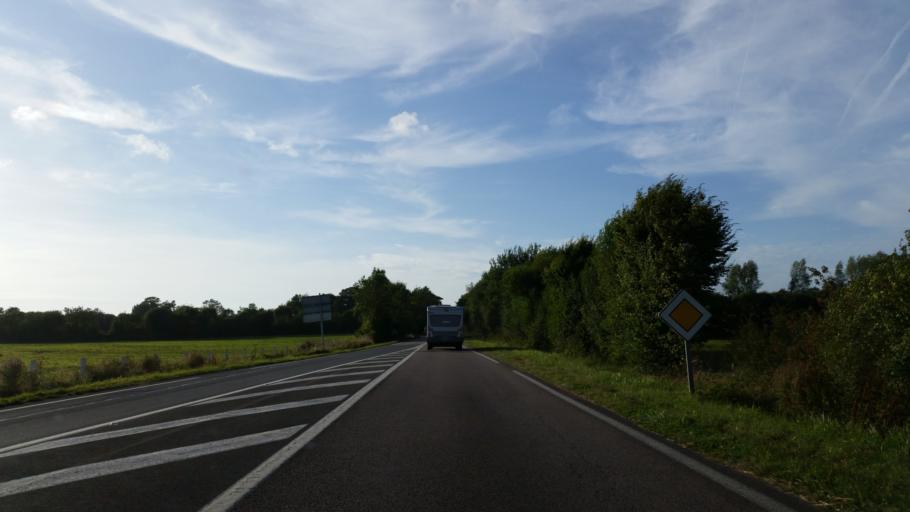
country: FR
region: Lower Normandy
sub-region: Departement du Calvados
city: Saint-Gatien-des-Bois
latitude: 49.3474
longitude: 0.1980
